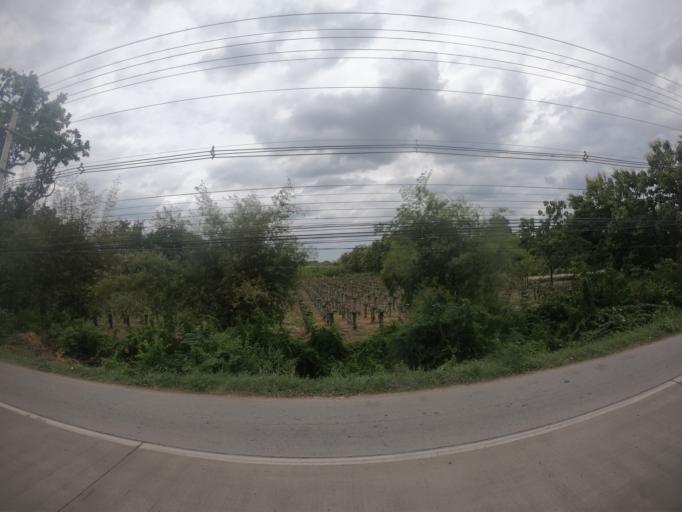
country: TH
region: Nakhon Ratchasima
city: Chok Chai
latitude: 14.7974
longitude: 102.1702
